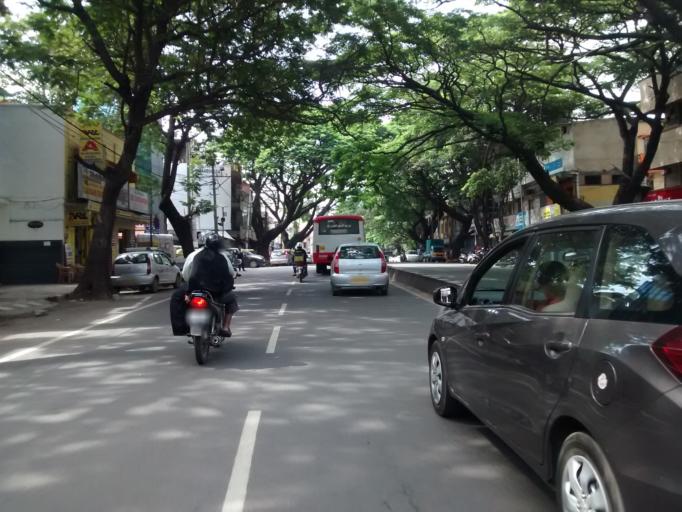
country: IN
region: Karnataka
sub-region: Bangalore Urban
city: Bangalore
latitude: 12.9997
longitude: 77.5526
